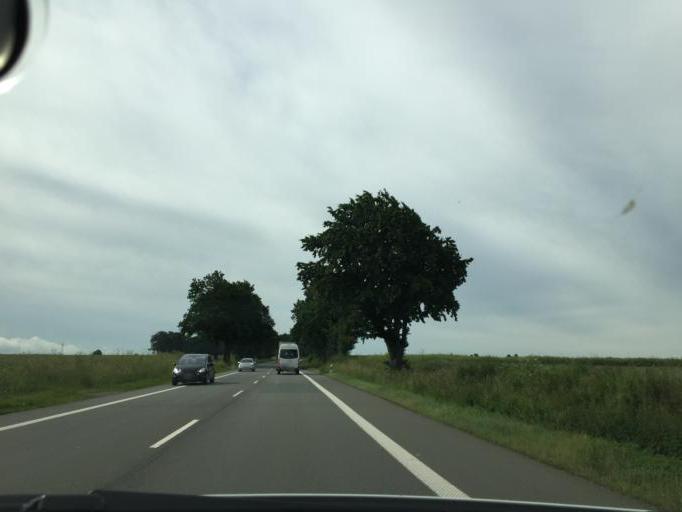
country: DE
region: North Rhine-Westphalia
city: Warburg
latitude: 51.5445
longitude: 9.1330
